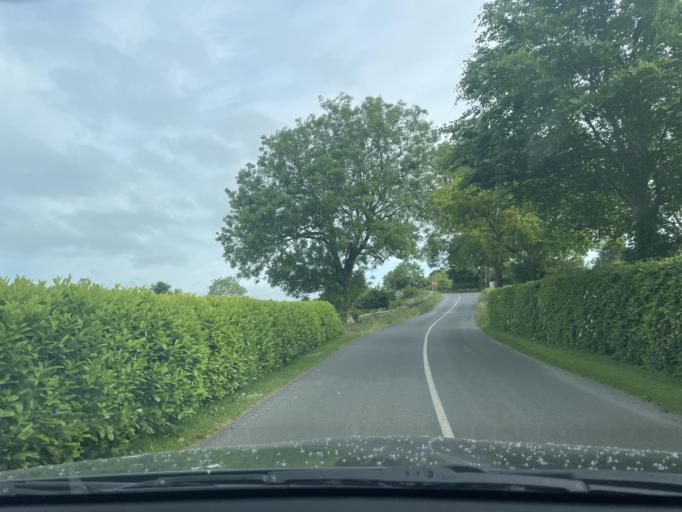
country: IE
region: Leinster
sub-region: County Carlow
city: Bagenalstown
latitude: 52.6662
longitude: -6.9637
